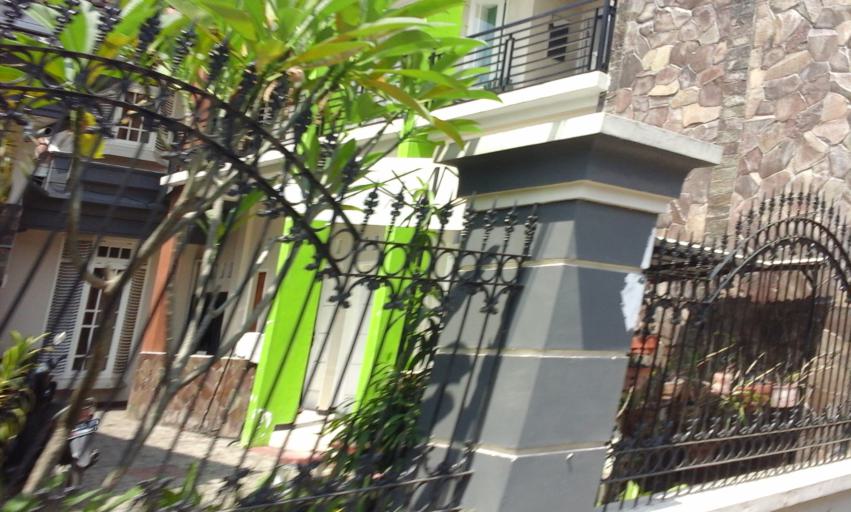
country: ID
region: East Java
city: Sumbersari Wetan
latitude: -8.1704
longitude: 113.7144
